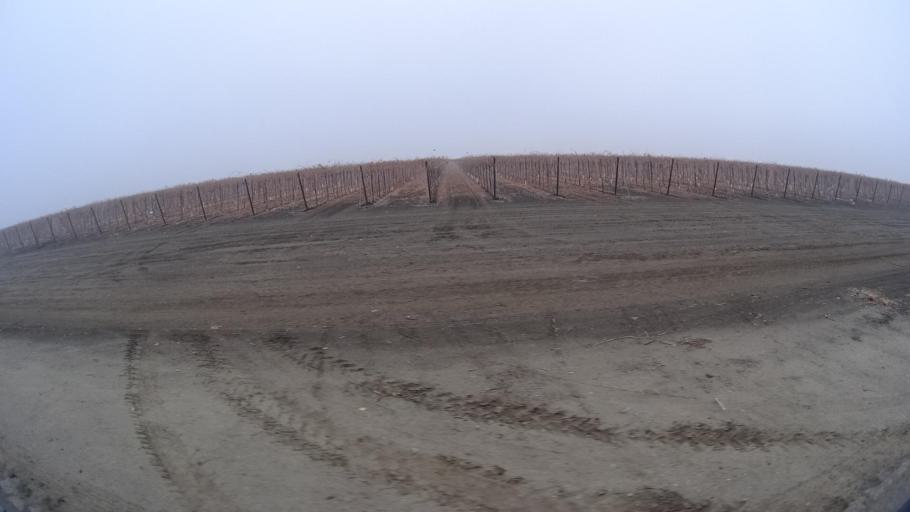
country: US
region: California
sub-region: Kern County
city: Buttonwillow
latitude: 35.4269
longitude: -119.5256
